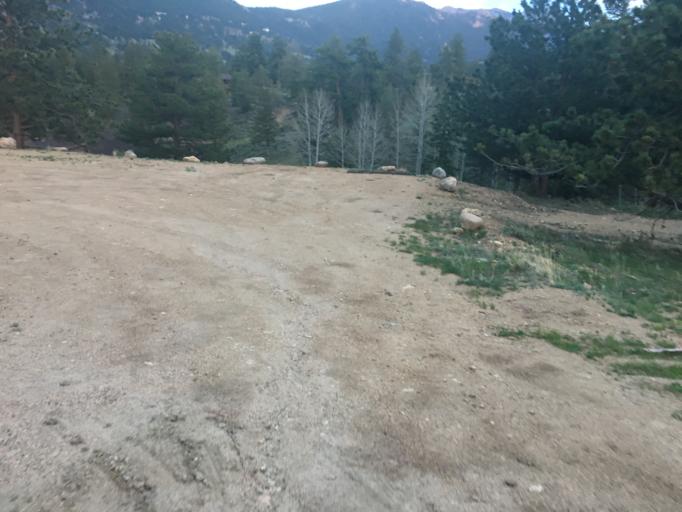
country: US
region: Colorado
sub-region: Larimer County
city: Estes Park
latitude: 40.3376
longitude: -105.5721
